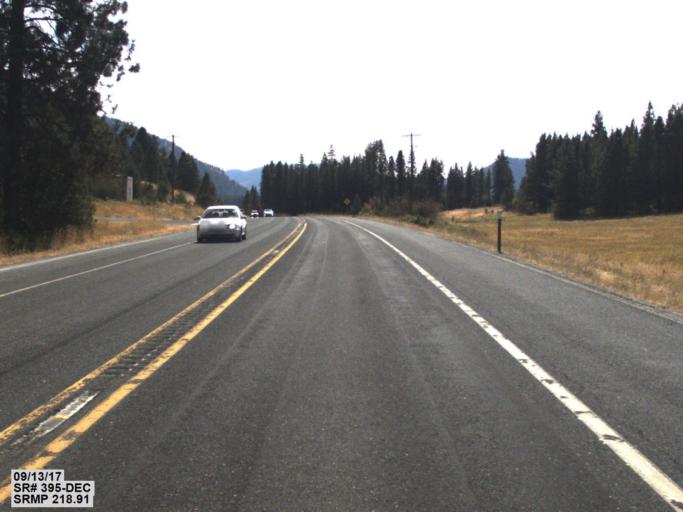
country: US
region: Washington
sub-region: Stevens County
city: Colville
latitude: 48.4004
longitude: -117.8498
